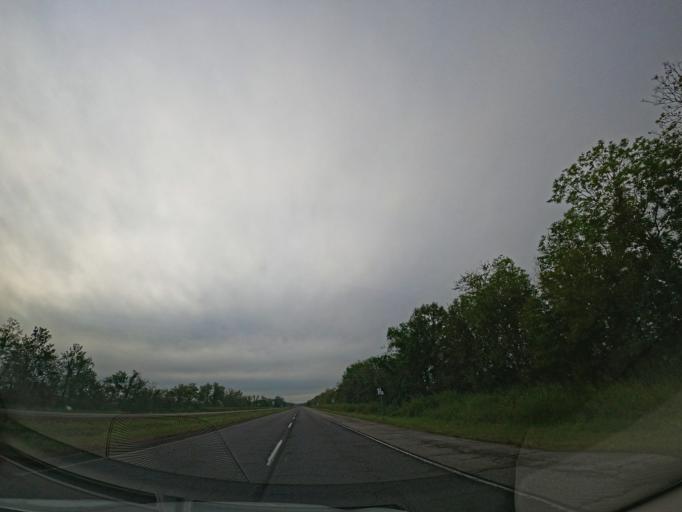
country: US
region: Louisiana
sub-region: Terrebonne Parish
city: Houma
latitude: 29.6542
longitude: -90.6784
